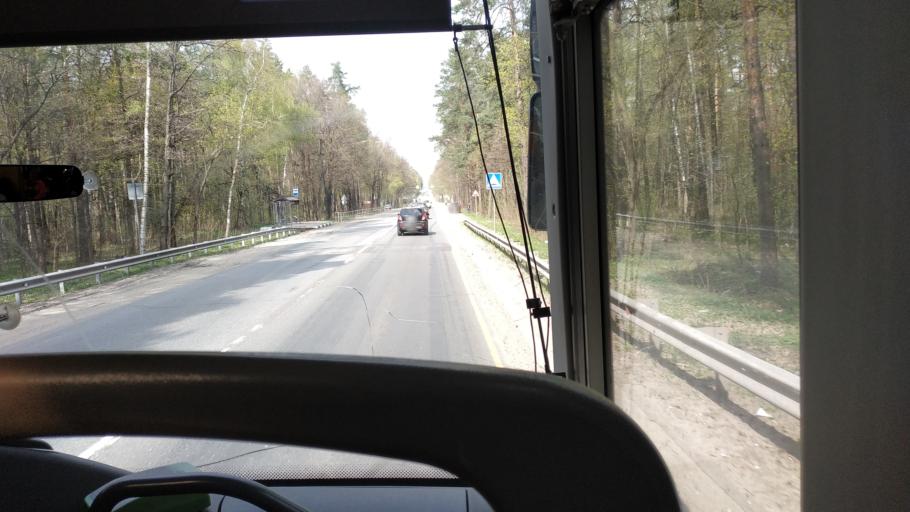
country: RU
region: Moskovskaya
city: Lytkarino
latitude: 55.6024
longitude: 37.9153
